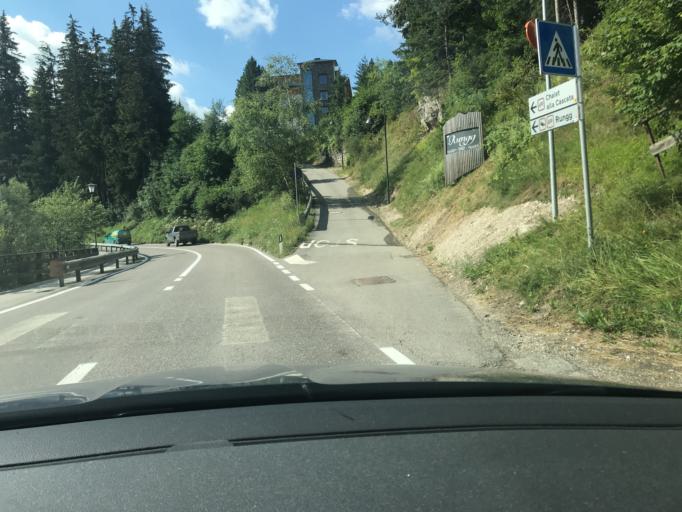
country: IT
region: Trentino-Alto Adige
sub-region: Bolzano
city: Badia
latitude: 46.6084
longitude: 11.8941
